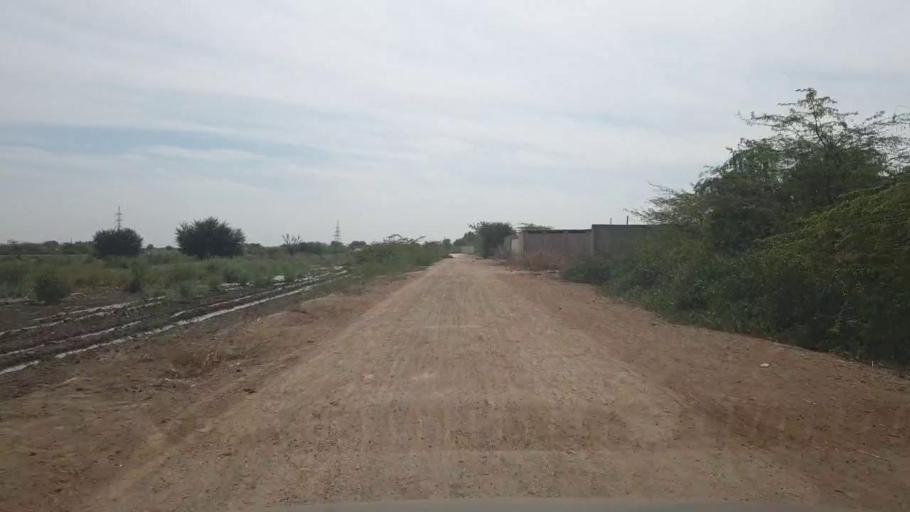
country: PK
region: Sindh
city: Kunri
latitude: 25.3016
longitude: 69.5657
